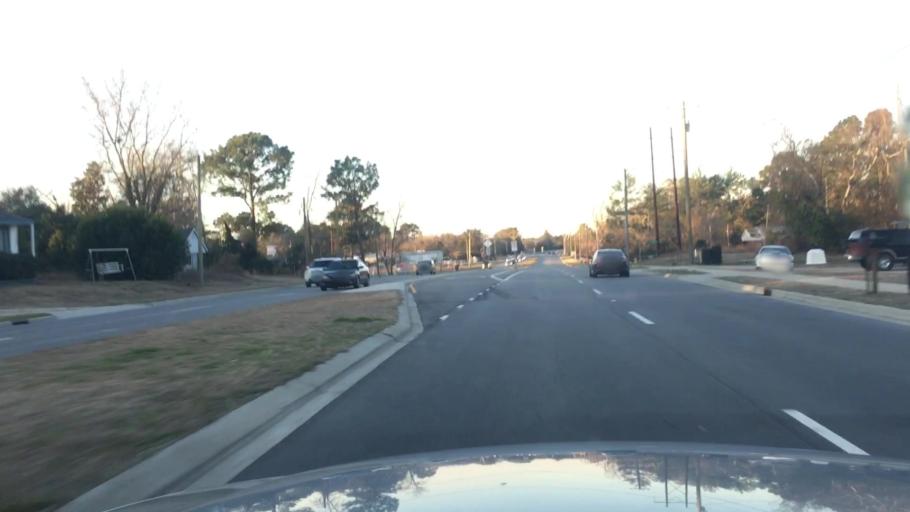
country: US
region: North Carolina
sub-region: Cumberland County
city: Hope Mills
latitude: 35.0024
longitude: -78.9260
